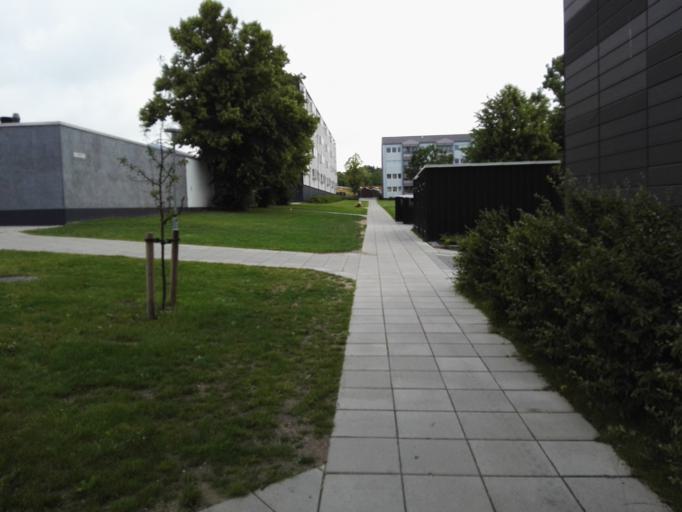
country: DK
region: Capital Region
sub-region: Ballerup Kommune
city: Ballerup
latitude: 55.7175
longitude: 12.3603
